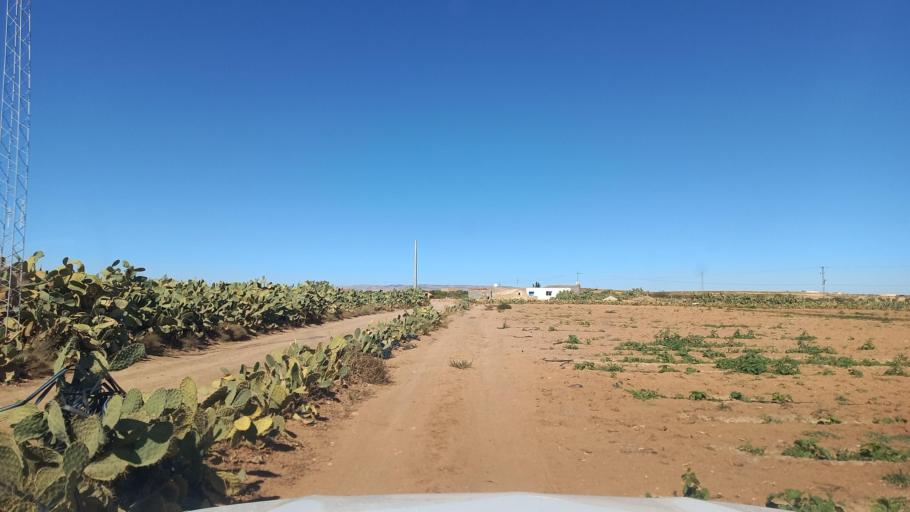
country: TN
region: Al Qasrayn
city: Sbiba
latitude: 35.3935
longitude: 9.0834
